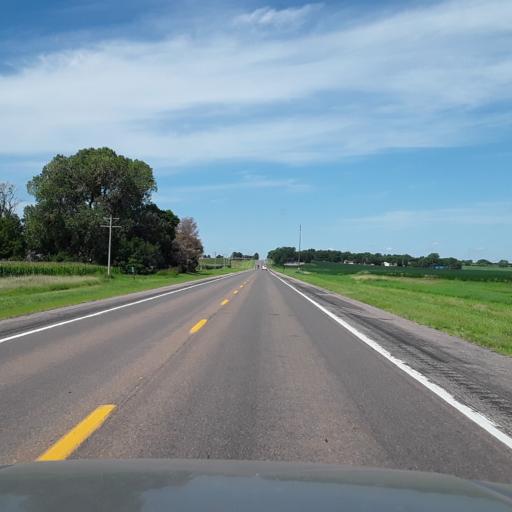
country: US
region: Nebraska
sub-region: Seward County
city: Seward
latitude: 40.9017
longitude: -97.1330
